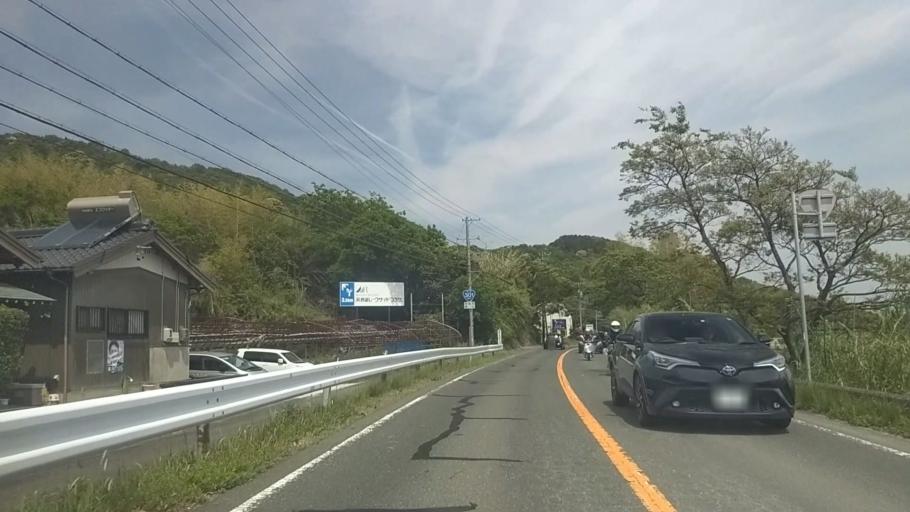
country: JP
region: Shizuoka
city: Kosai-shi
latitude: 34.7691
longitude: 137.5377
